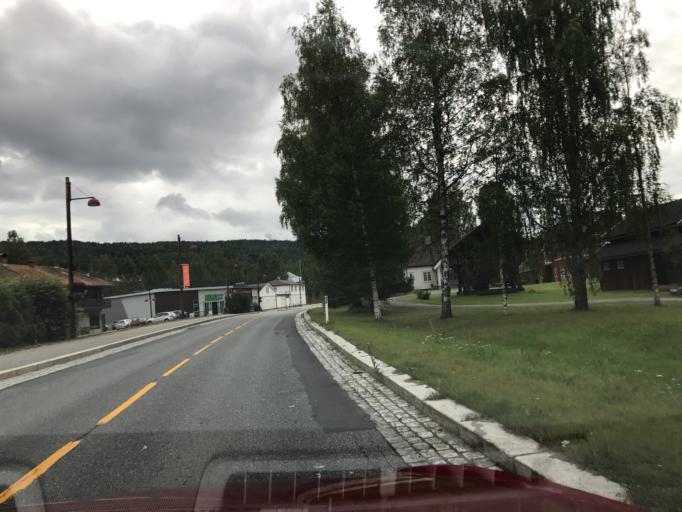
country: NO
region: Buskerud
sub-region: Flesberg
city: Lampeland
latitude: 59.8362
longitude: 9.5768
